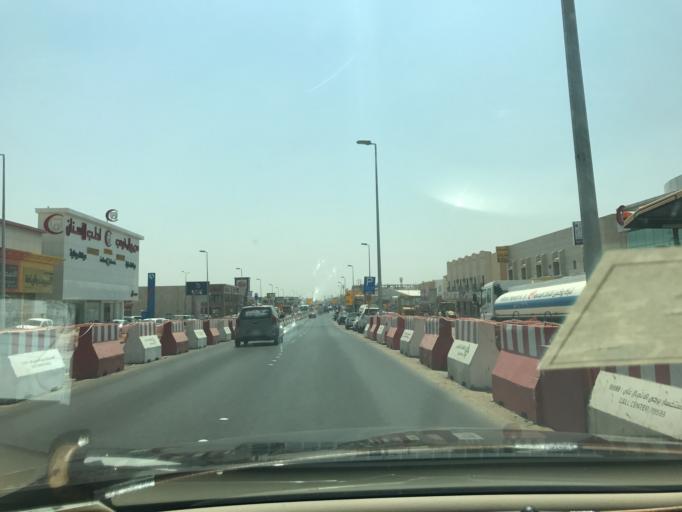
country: SA
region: Ar Riyad
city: Riyadh
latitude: 24.7513
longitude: 46.7714
